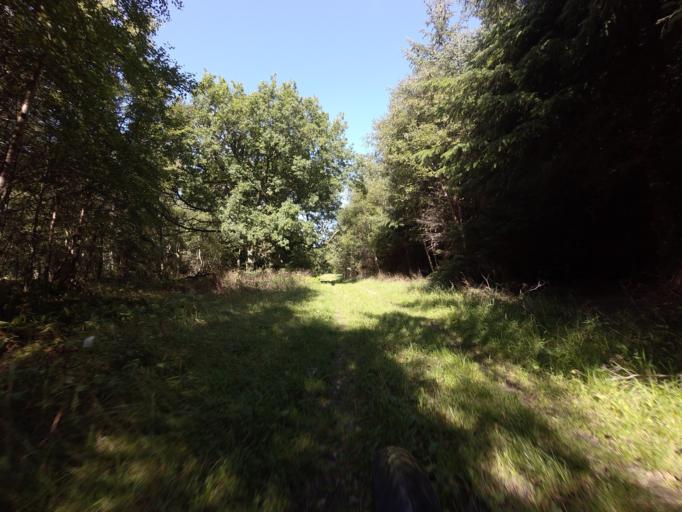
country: DK
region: North Denmark
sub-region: Hjorring Kommune
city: Hirtshals
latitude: 57.5849
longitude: 10.0031
